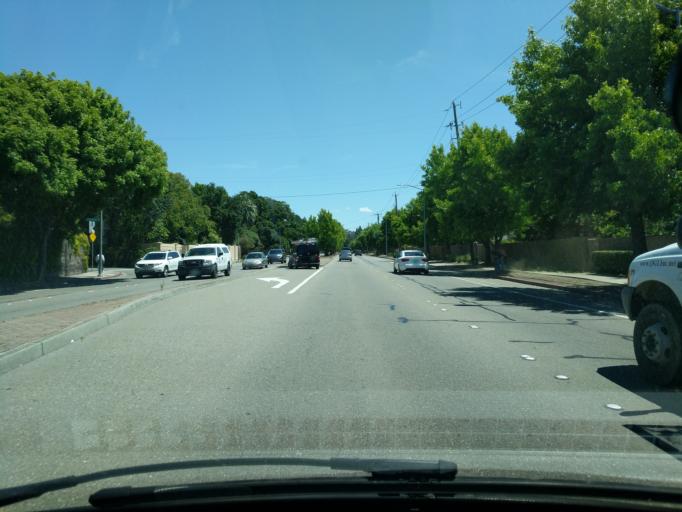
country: US
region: California
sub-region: Contra Costa County
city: Waldon
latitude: 37.9269
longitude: -122.0405
